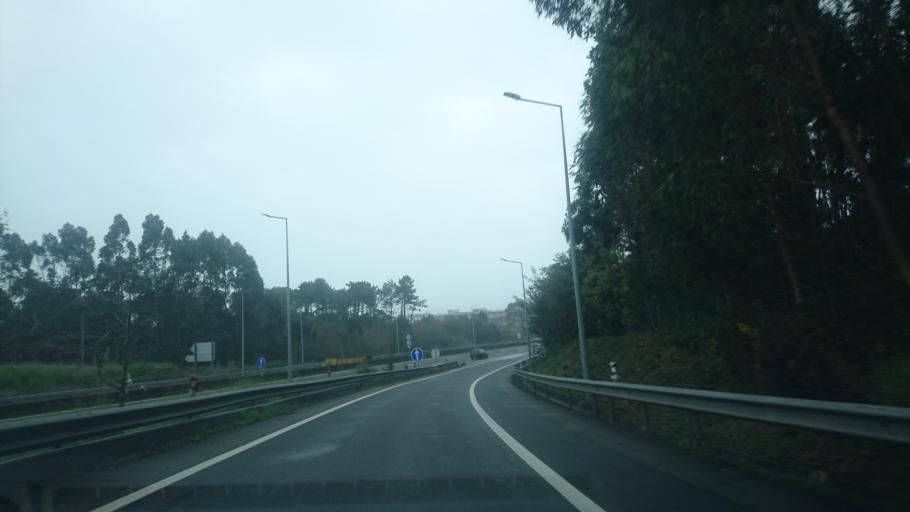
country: PT
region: Porto
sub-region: Vila Nova de Gaia
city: Gulpilhares
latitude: 41.0805
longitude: -8.6319
